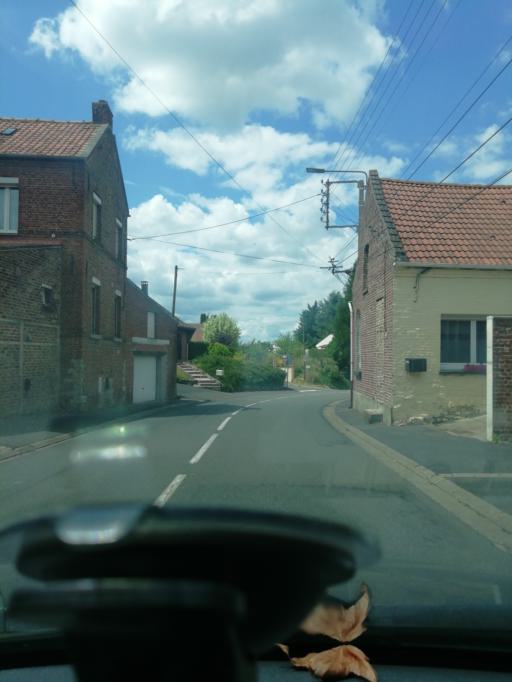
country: FR
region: Nord-Pas-de-Calais
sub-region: Departement du Nord
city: Monchecourt
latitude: 50.3033
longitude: 3.1788
